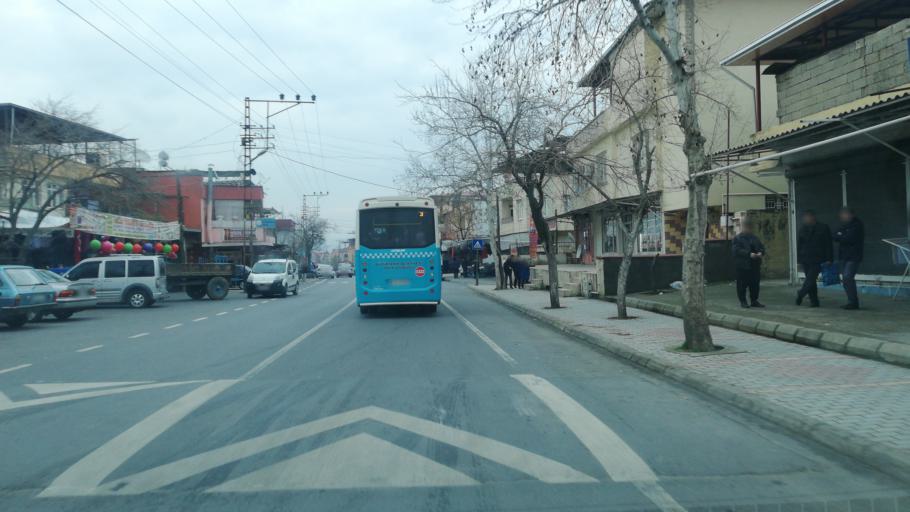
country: TR
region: Kahramanmaras
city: Kahramanmaras
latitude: 37.5713
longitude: 36.9507
